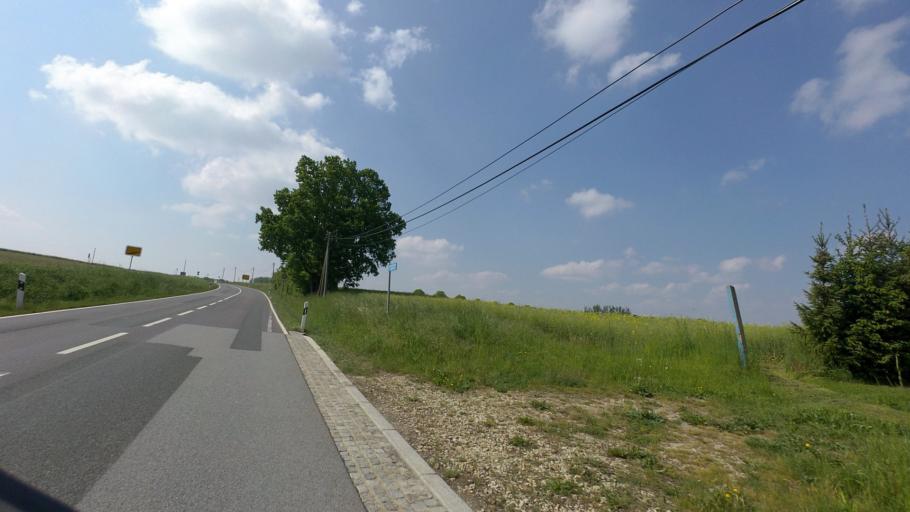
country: DE
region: Saxony
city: Weissenberg
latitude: 51.1888
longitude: 14.6231
